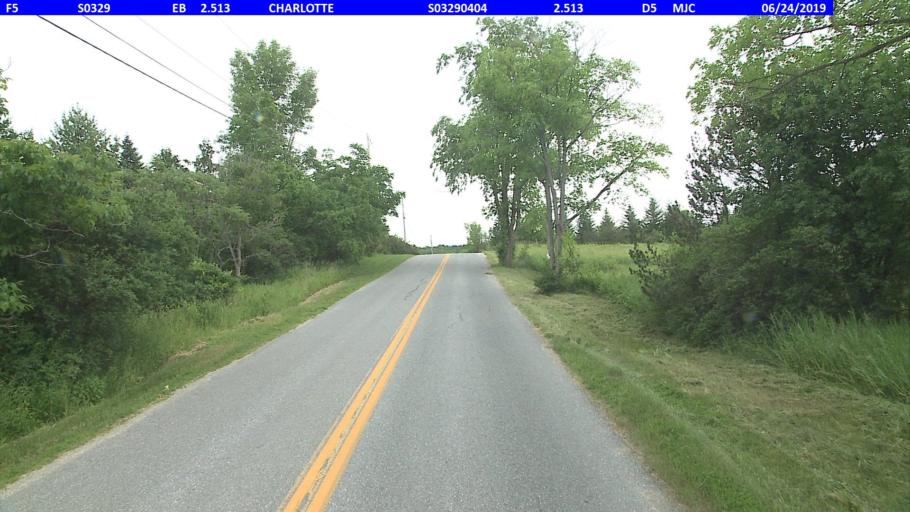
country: US
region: Vermont
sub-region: Addison County
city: Vergennes
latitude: 44.3050
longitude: -73.2939
